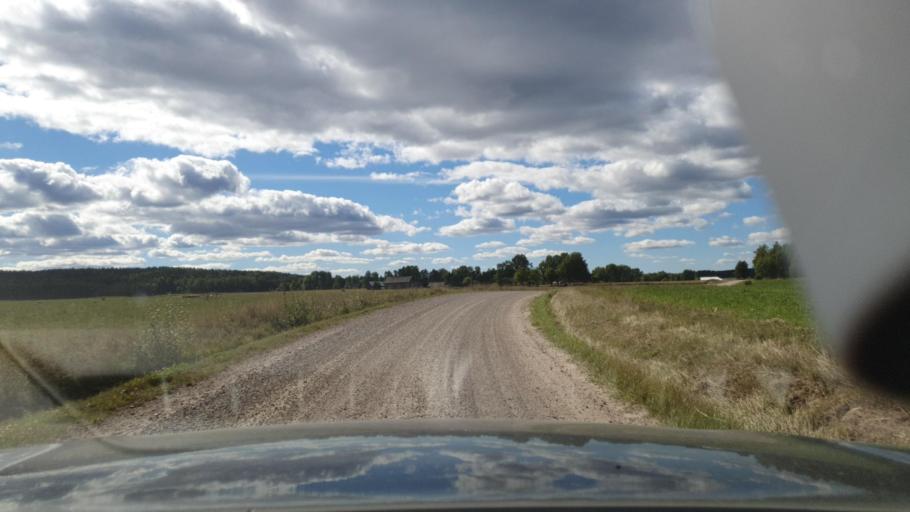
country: SE
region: Vaermland
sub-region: Karlstads Kommun
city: Molkom
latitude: 59.5597
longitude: 13.7094
